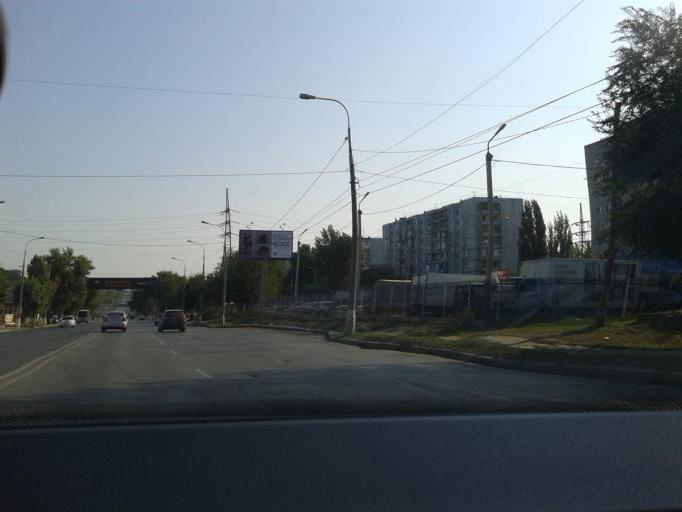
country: RU
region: Volgograd
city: Volgograd
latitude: 48.7044
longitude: 44.4825
